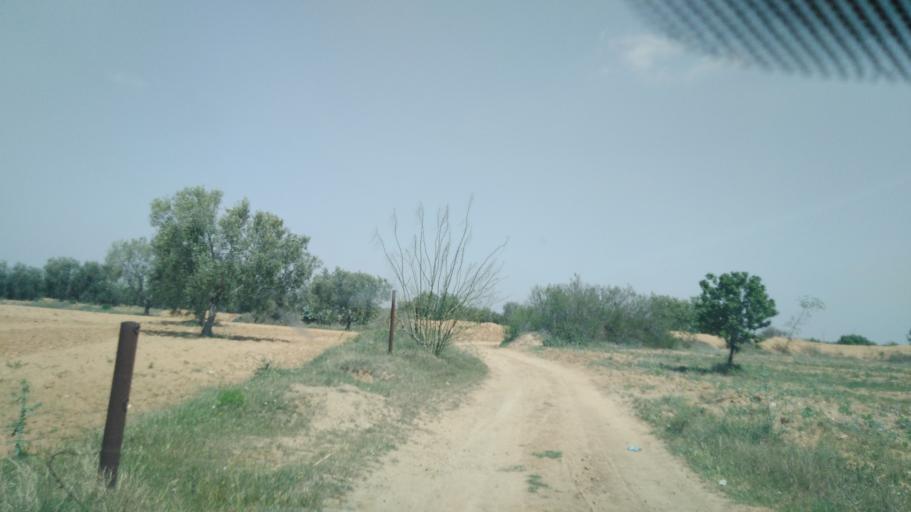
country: TN
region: Safaqis
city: Sfax
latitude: 34.7338
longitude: 10.5744
